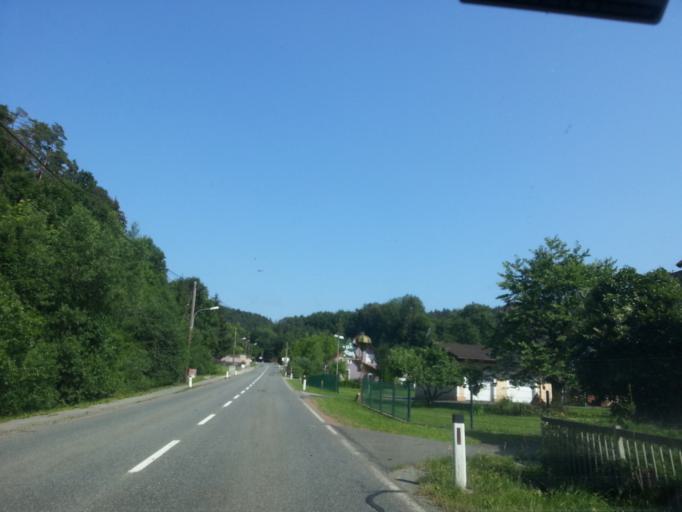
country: AT
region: Styria
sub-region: Politischer Bezirk Leibnitz
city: Grossklein
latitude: 46.7351
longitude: 15.4478
